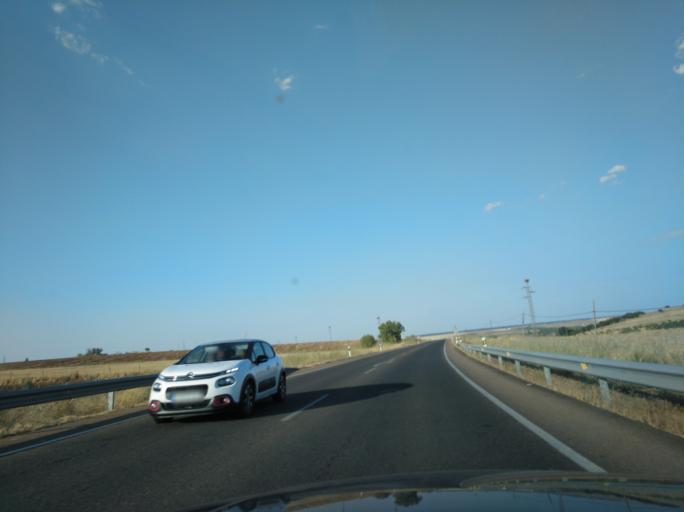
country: ES
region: Extremadura
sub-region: Provincia de Badajoz
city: Olivenza
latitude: 38.7239
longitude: -7.0801
